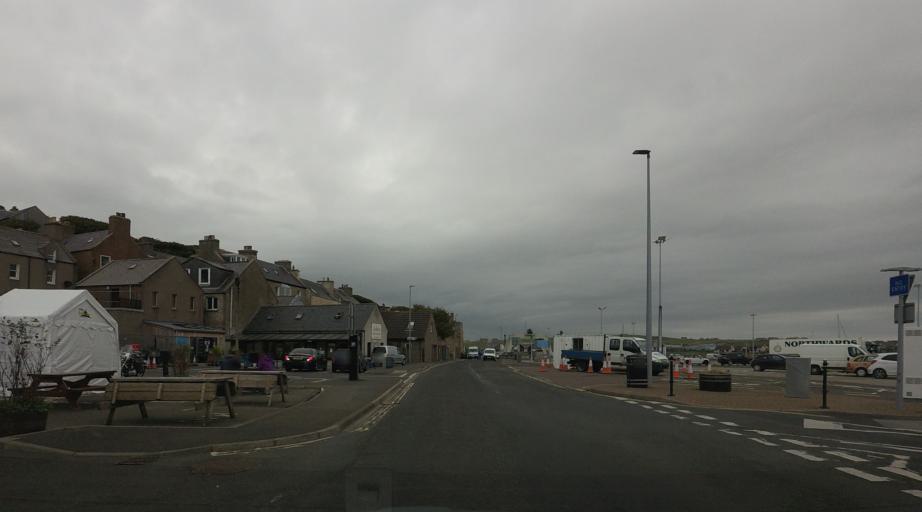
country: GB
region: Scotland
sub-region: Orkney Islands
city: Stromness
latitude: 58.9640
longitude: -3.2968
